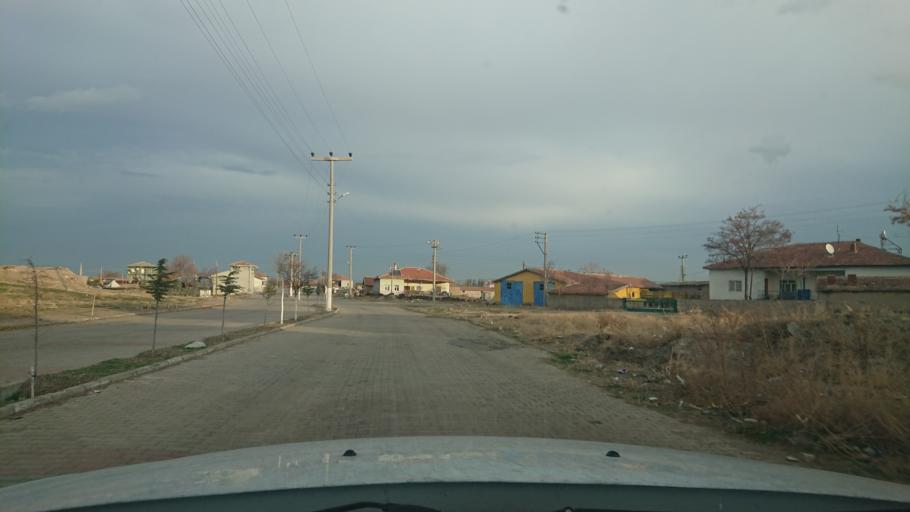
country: TR
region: Aksaray
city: Yesilova
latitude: 38.4121
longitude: 33.8389
